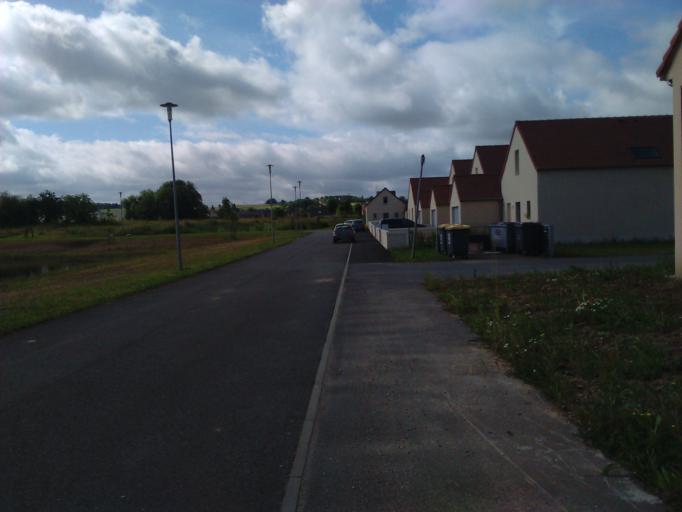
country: FR
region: Centre
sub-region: Departement du Loir-et-Cher
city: Naveil
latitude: 47.7942
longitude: 1.0351
